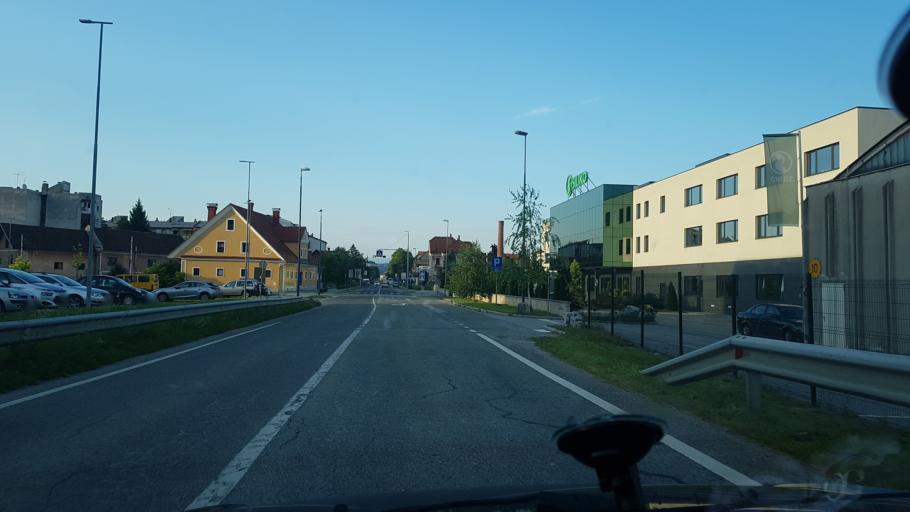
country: SI
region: Vrhnika
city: Vrhnika
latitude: 45.9592
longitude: 14.2932
